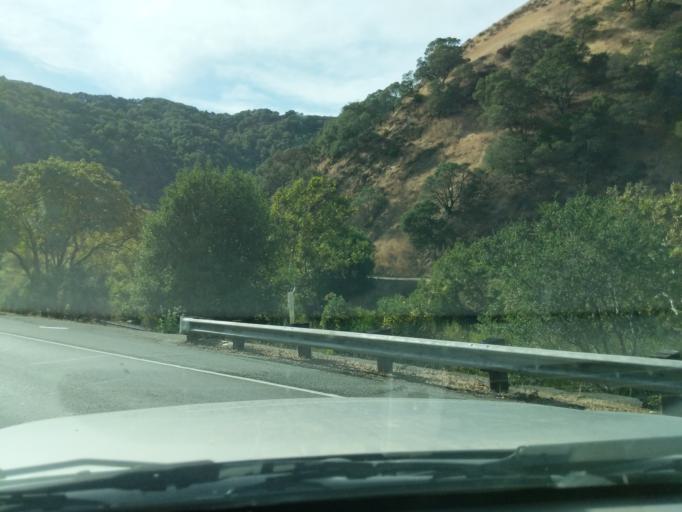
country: US
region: California
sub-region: Alameda County
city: Fremont
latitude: 37.5939
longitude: -121.9311
